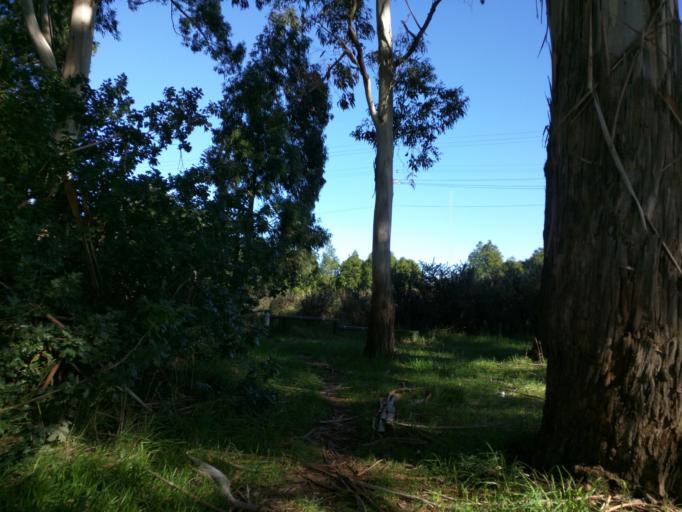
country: NZ
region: Canterbury
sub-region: Selwyn District
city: Lincoln
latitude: -43.6437
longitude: 172.4579
